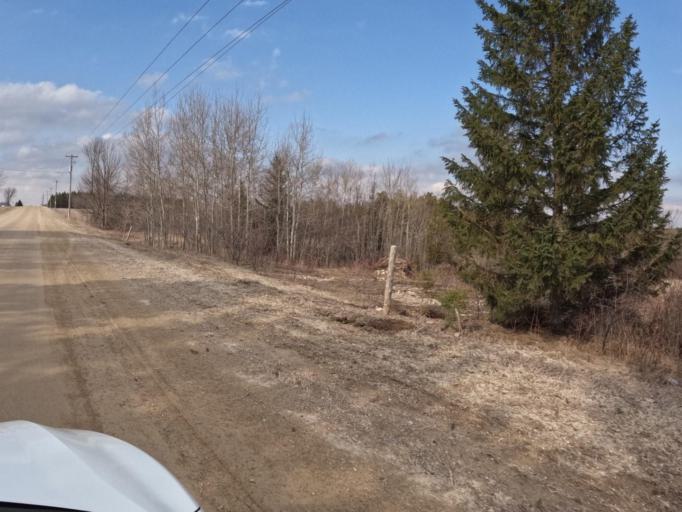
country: CA
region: Ontario
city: Orangeville
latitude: 43.8985
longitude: -80.3009
